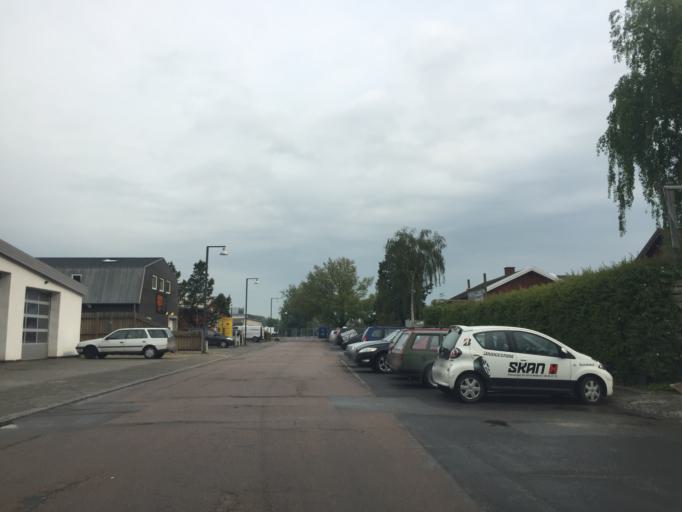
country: DK
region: Capital Region
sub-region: Rodovre Kommune
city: Rodovre
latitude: 55.6719
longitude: 12.4428
